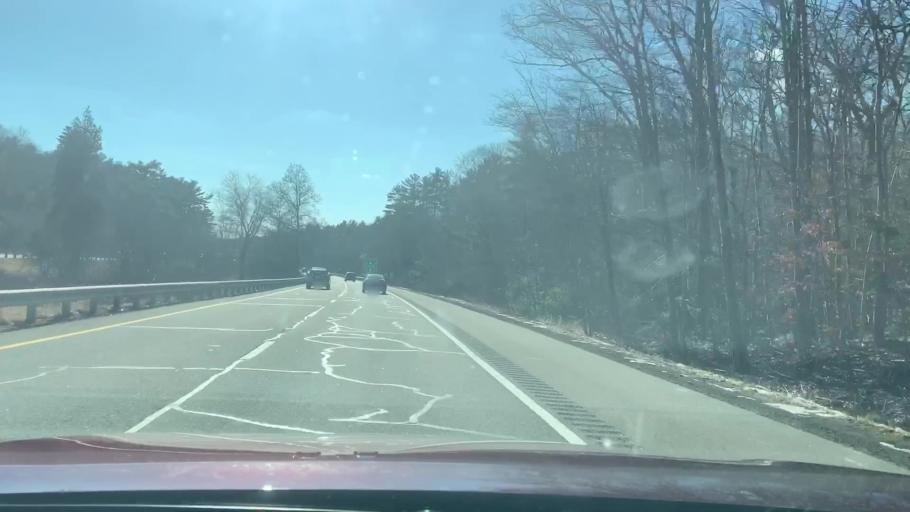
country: US
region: Massachusetts
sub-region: Essex County
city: Essex
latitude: 42.6012
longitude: -70.7470
